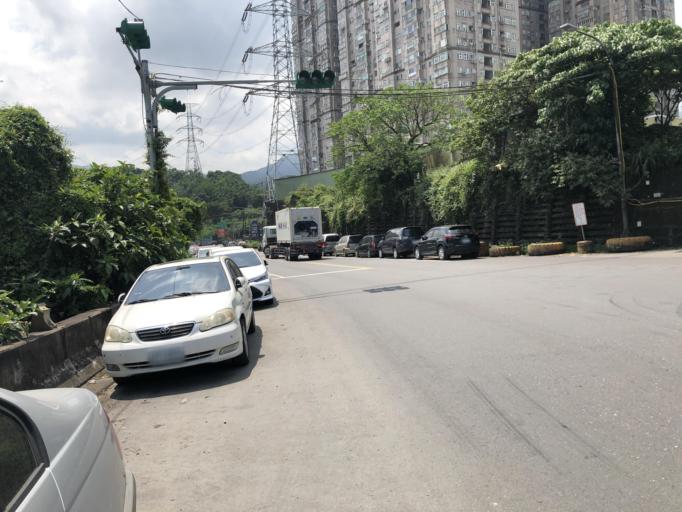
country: TW
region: Taiwan
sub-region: Keelung
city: Keelung
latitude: 25.0768
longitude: 121.6822
